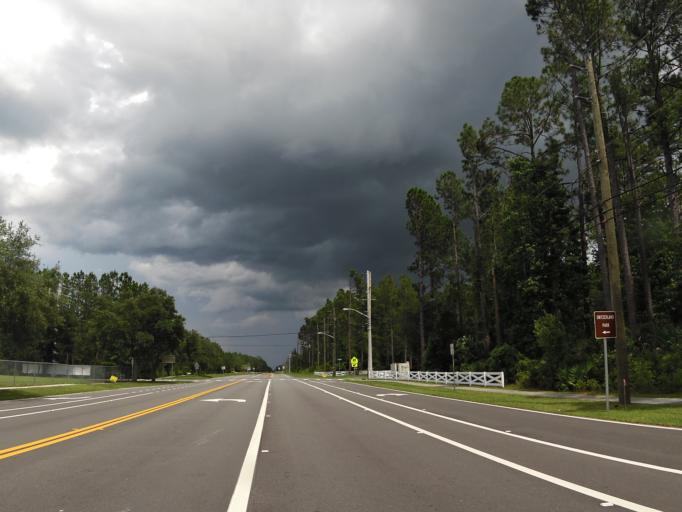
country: US
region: Florida
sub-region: Saint Johns County
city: Fruit Cove
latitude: 30.0617
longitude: -81.6477
